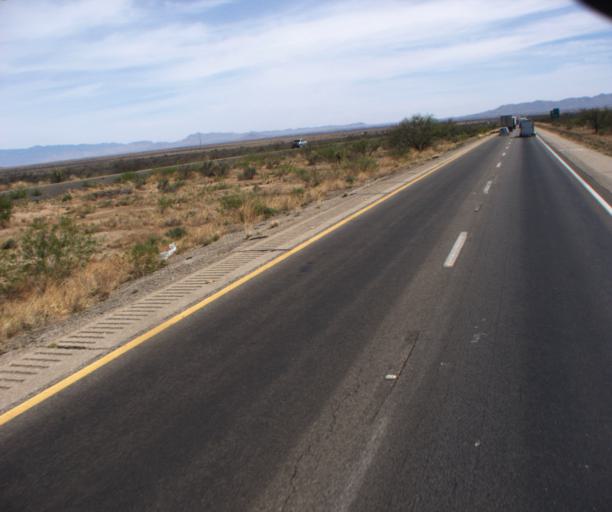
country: US
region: Arizona
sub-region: Cochise County
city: Willcox
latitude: 32.1646
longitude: -109.9689
